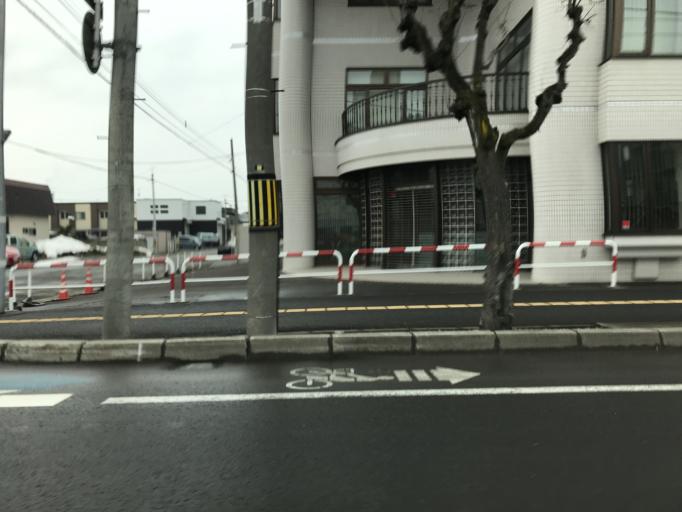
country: JP
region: Hokkaido
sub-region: Asahikawa-shi
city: Asahikawa
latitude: 43.7711
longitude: 142.3516
